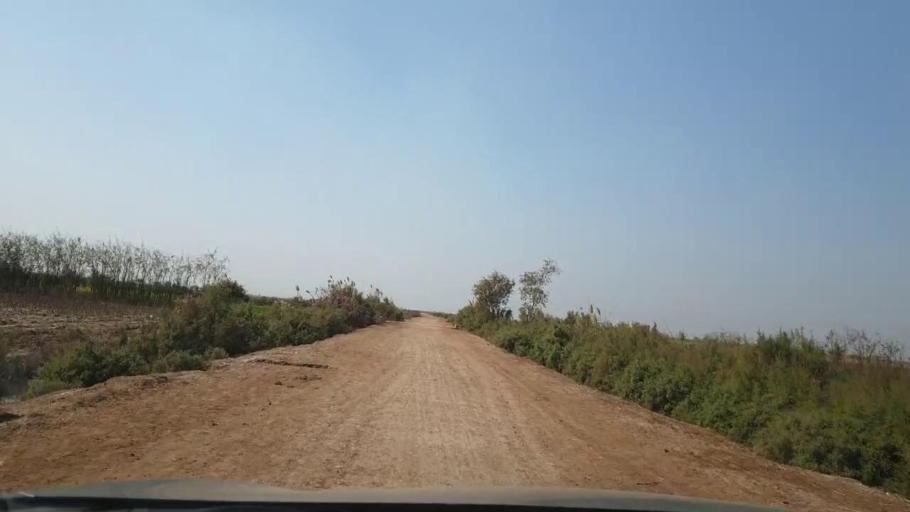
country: PK
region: Sindh
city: Berani
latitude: 25.6629
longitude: 68.8857
